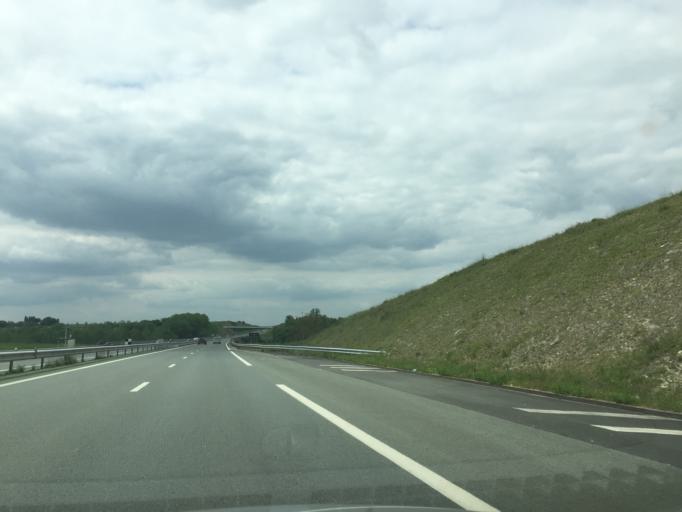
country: FR
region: Poitou-Charentes
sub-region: Departement des Deux-Sevres
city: Saint-Maxire
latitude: 46.4219
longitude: -0.4473
